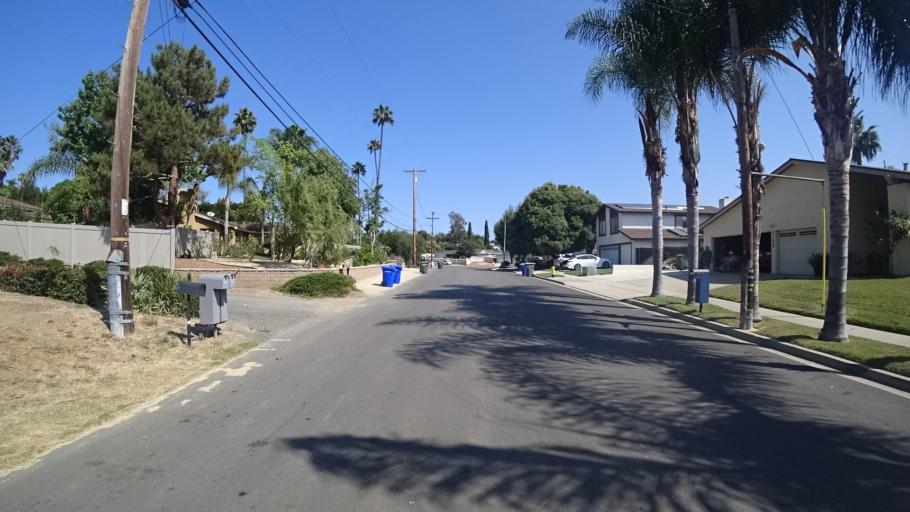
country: US
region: California
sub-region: San Diego County
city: Vista
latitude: 33.1750
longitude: -117.2183
